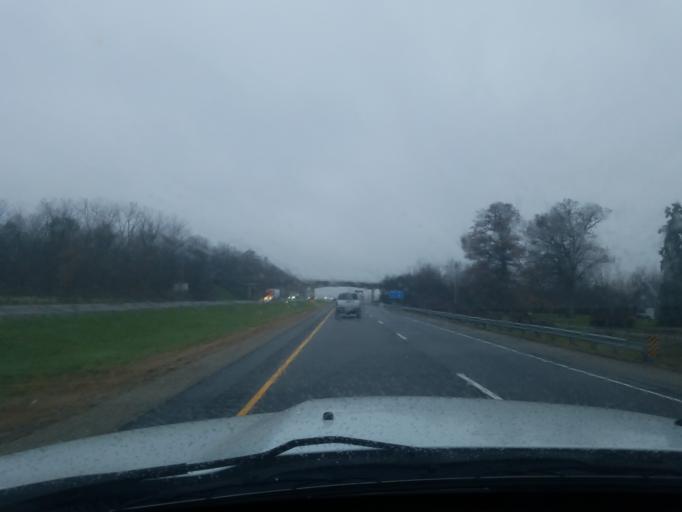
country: US
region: Indiana
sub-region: Grant County
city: Fairmount
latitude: 40.3660
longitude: -85.5590
